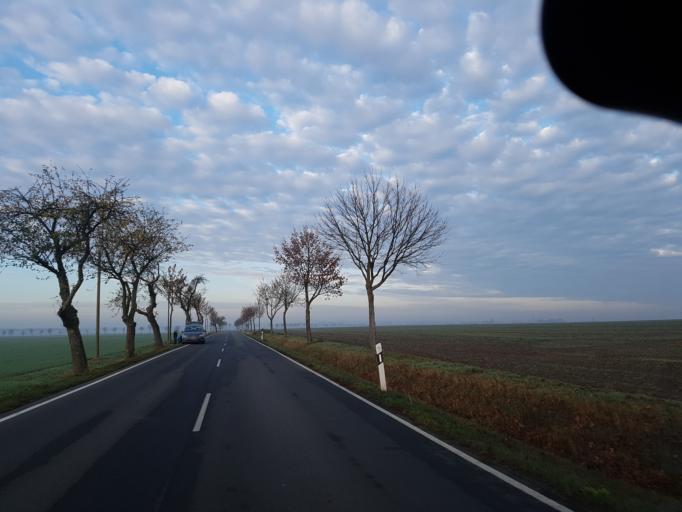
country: DE
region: Saxony-Anhalt
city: Zahna
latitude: 51.9035
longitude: 12.8270
